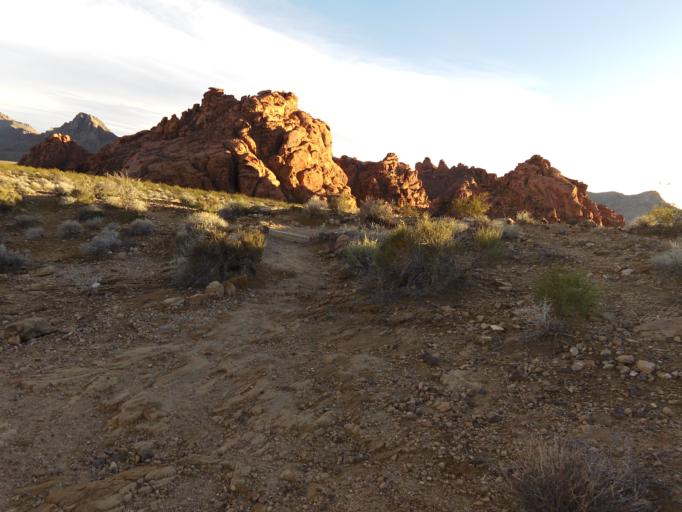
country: US
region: Nevada
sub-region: Clark County
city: Moapa Valley
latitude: 36.4220
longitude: -114.5400
